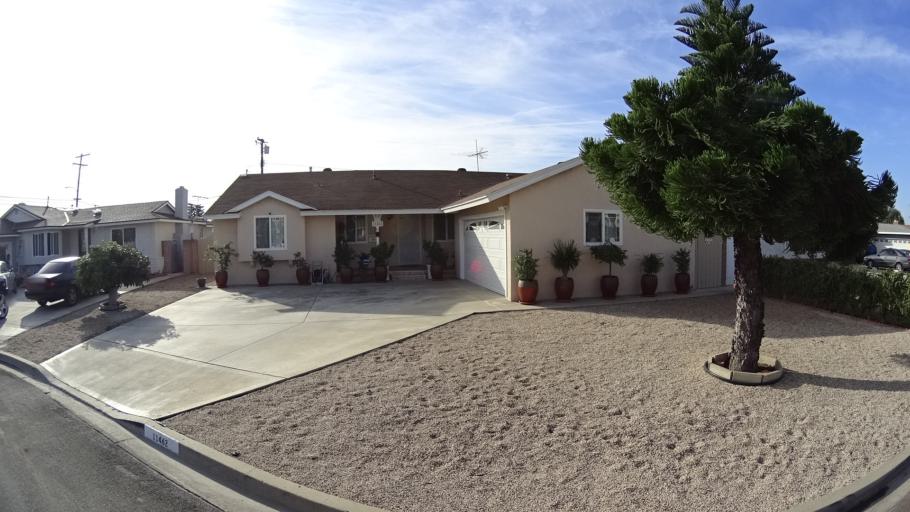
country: US
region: California
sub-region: Orange County
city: Garden Grove
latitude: 33.7922
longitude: -117.9330
